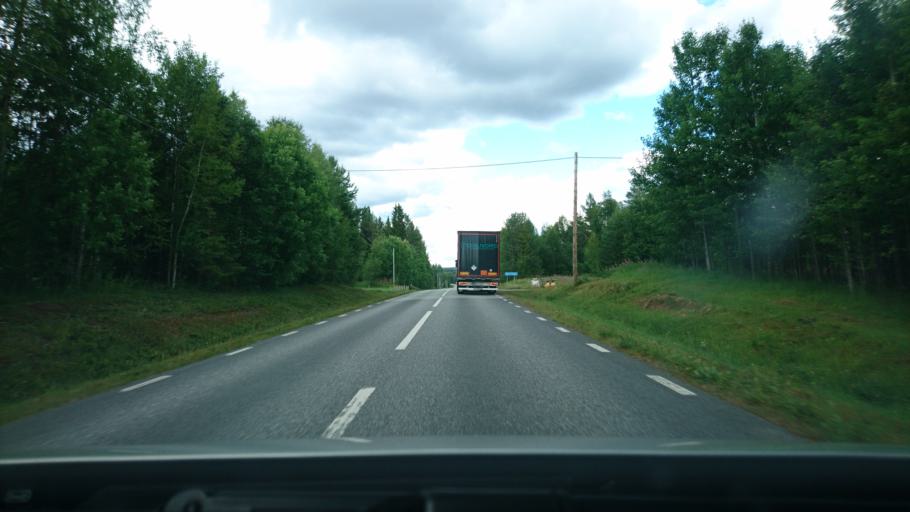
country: SE
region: Vaesterbotten
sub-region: Asele Kommun
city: Asele
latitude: 63.8694
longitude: 17.1850
